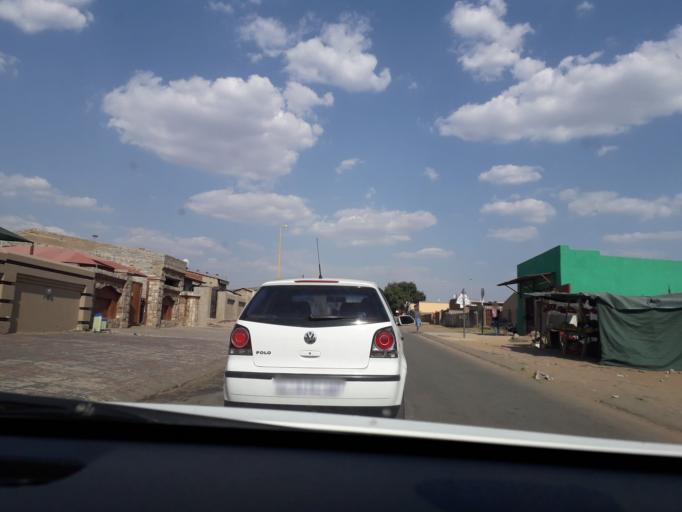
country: ZA
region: Gauteng
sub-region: Ekurhuleni Metropolitan Municipality
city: Tembisa
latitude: -26.0132
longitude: 28.2238
